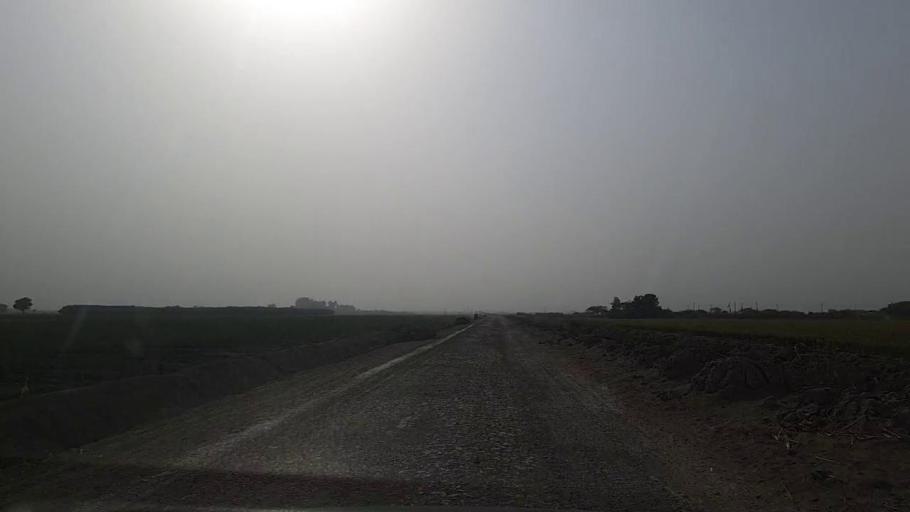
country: PK
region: Sindh
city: Pithoro
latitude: 25.4306
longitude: 69.2995
